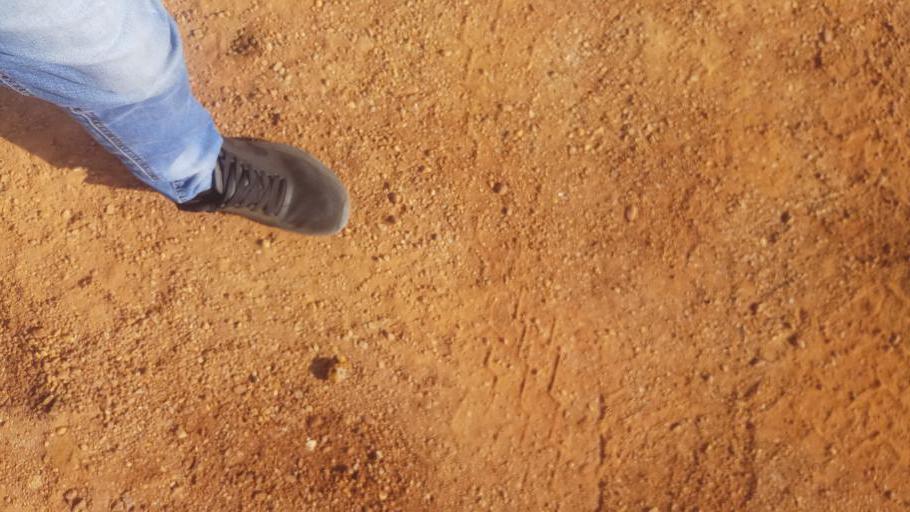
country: ET
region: Gambela
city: Gambela
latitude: 8.1318
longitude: 34.2981
